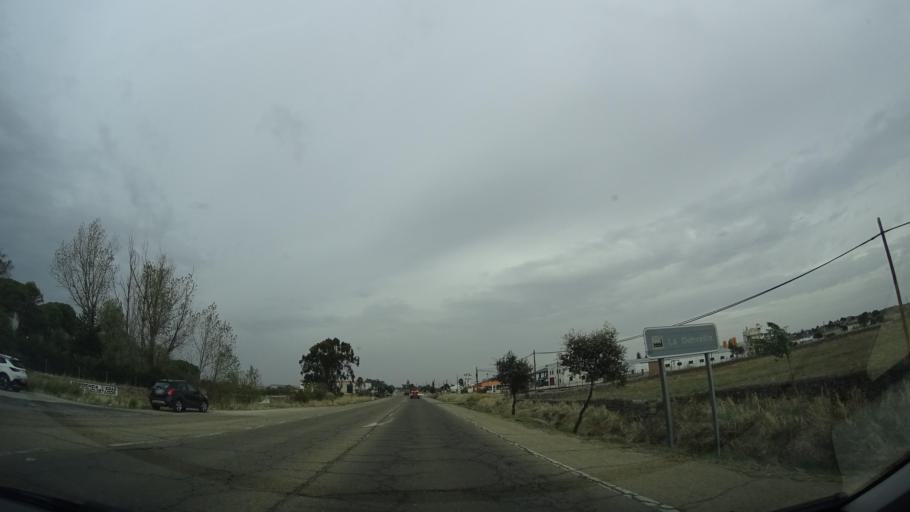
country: ES
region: Extremadura
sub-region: Provincia de Caceres
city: Trujillo
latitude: 39.4736
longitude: -5.8597
